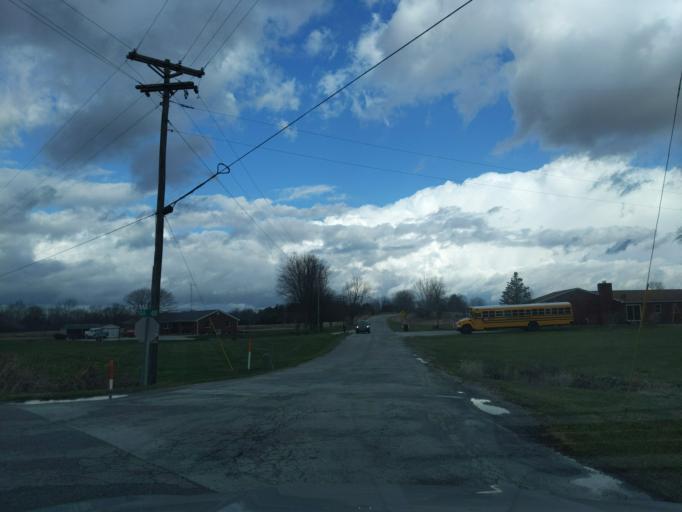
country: US
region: Indiana
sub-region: Decatur County
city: Saint Paul
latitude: 39.4018
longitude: -85.5597
